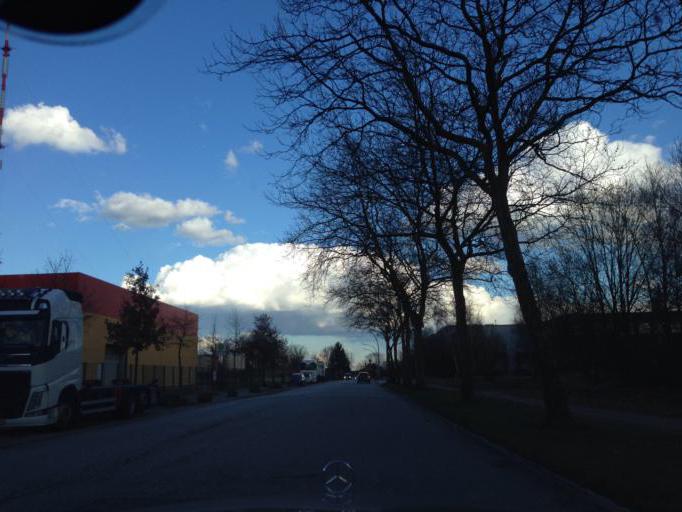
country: DE
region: Hamburg
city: Wandsbek
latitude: 53.5197
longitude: 10.0955
